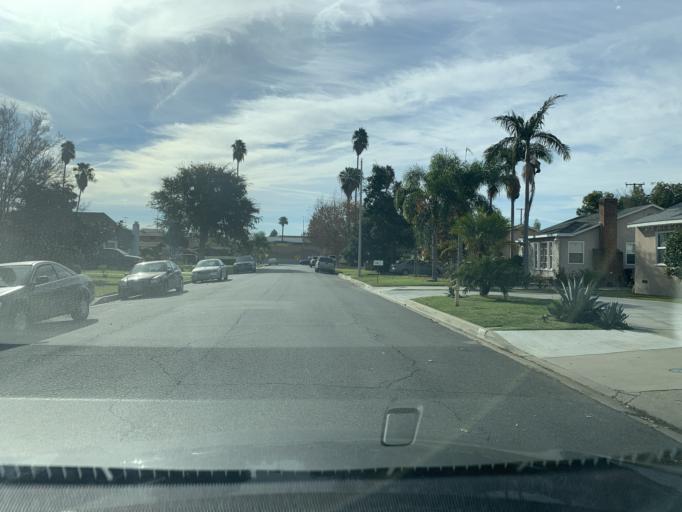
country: US
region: California
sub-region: Los Angeles County
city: West Covina
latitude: 34.0740
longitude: -117.9322
